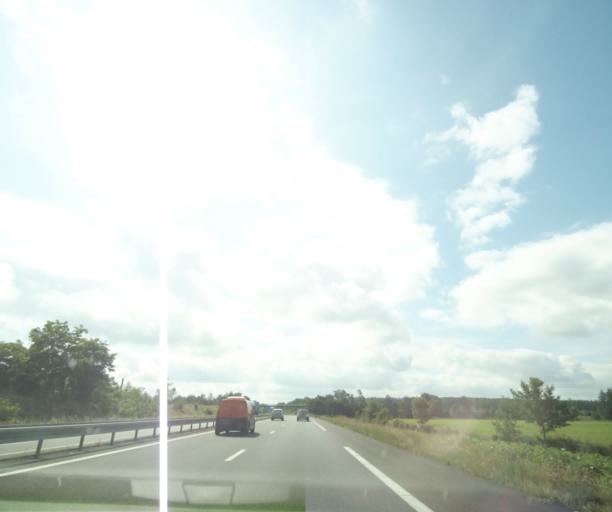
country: FR
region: Pays de la Loire
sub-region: Departement de Maine-et-Loire
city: Jumelles
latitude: 47.3942
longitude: -0.1107
